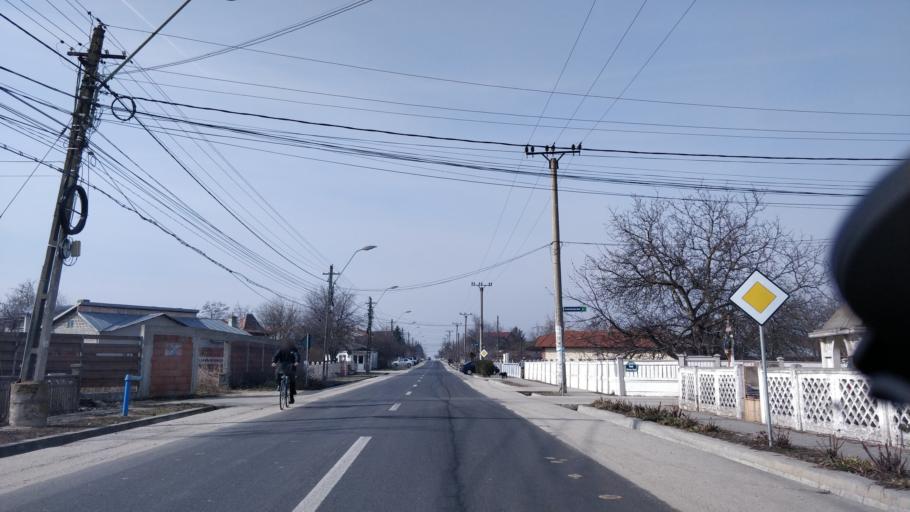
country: RO
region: Giurgiu
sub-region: Comuna Bolintin Deal
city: Bolintin Deal
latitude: 44.4608
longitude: 25.8098
